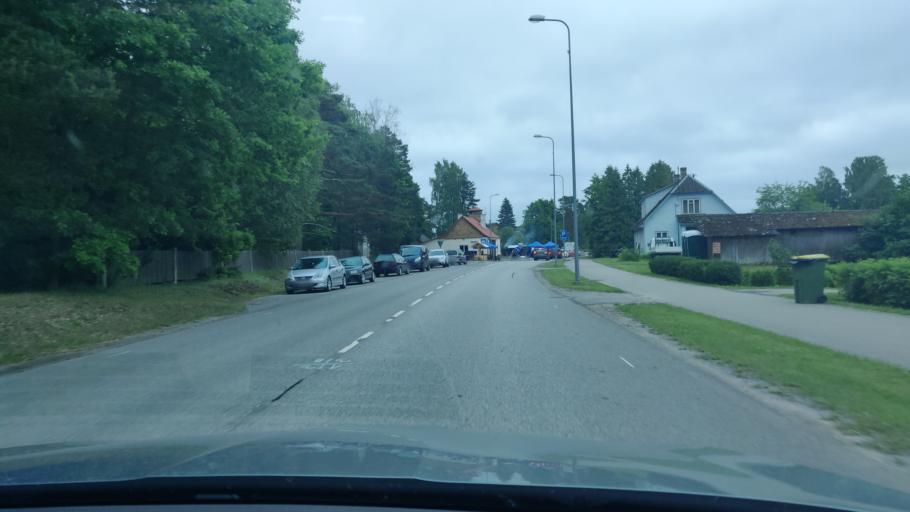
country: EE
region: Vorumaa
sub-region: Voru linn
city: Voru
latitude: 57.7349
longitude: 27.2819
